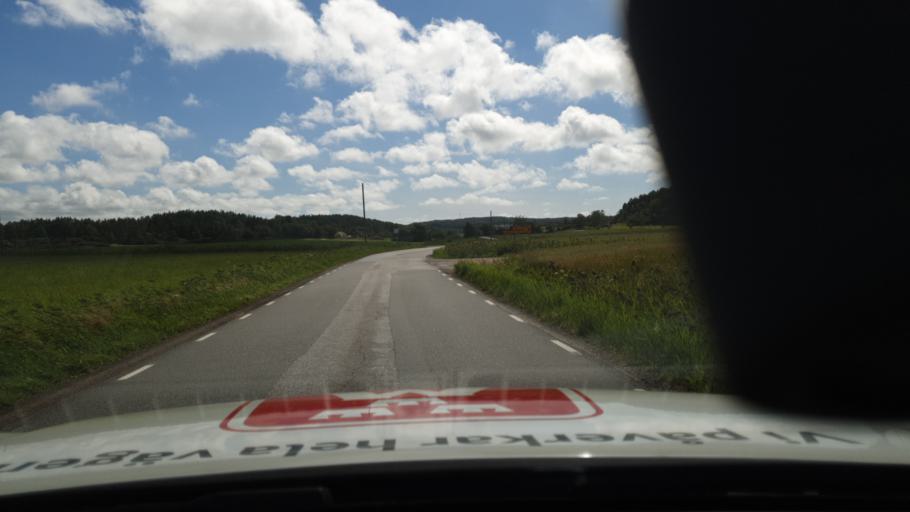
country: SE
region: Vaestra Goetaland
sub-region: Orust
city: Henan
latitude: 58.1397
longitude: 11.5647
